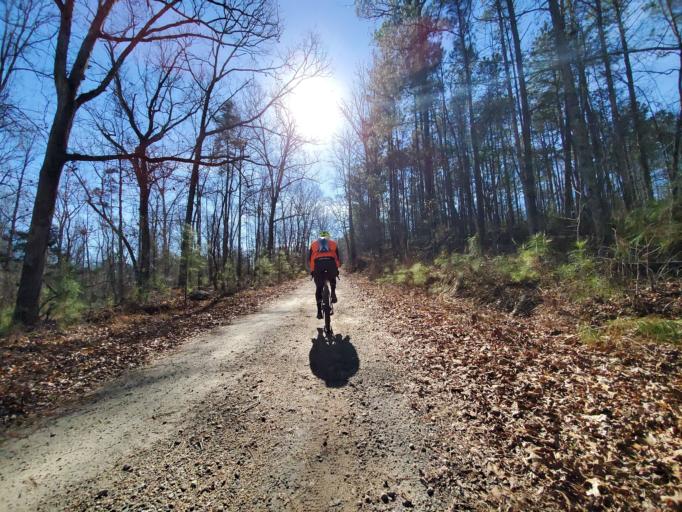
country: US
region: Georgia
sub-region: Fulton County
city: Chattahoochee Hills
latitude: 33.5689
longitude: -84.7540
